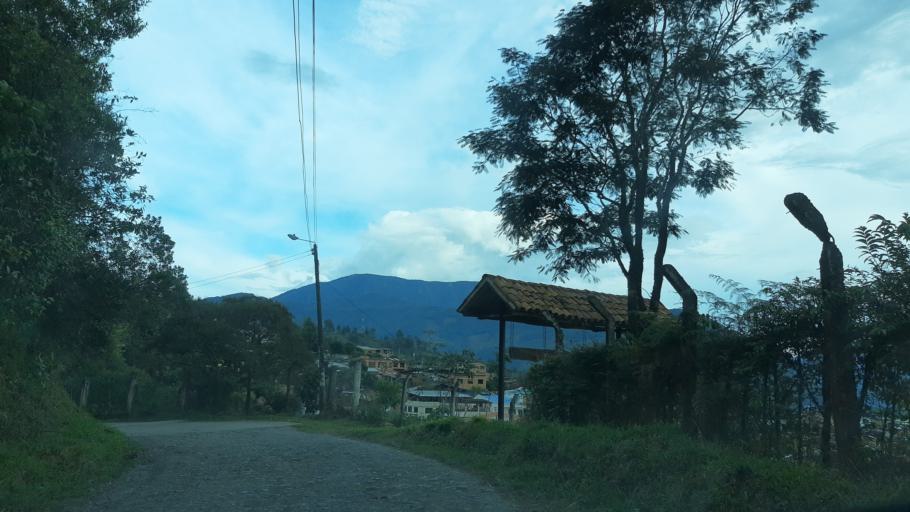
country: CO
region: Boyaca
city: Chivor
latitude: 4.9736
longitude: -73.3202
